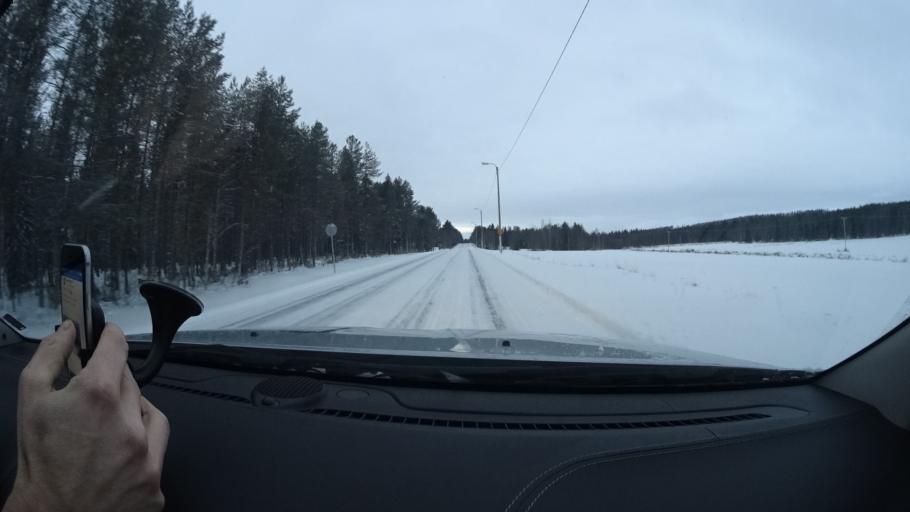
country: FI
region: Northern Ostrobothnia
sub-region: Koillismaa
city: Kuusamo
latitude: 66.0949
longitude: 28.7131
